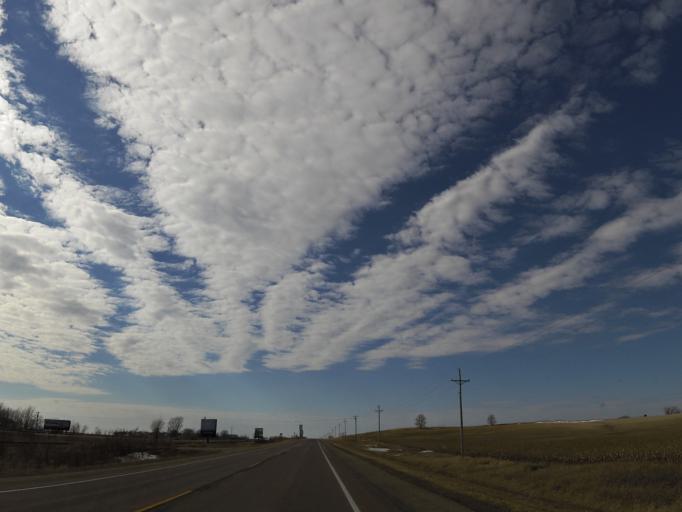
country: US
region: Minnesota
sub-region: Waseca County
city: Waseca
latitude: 44.0966
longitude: -93.5847
